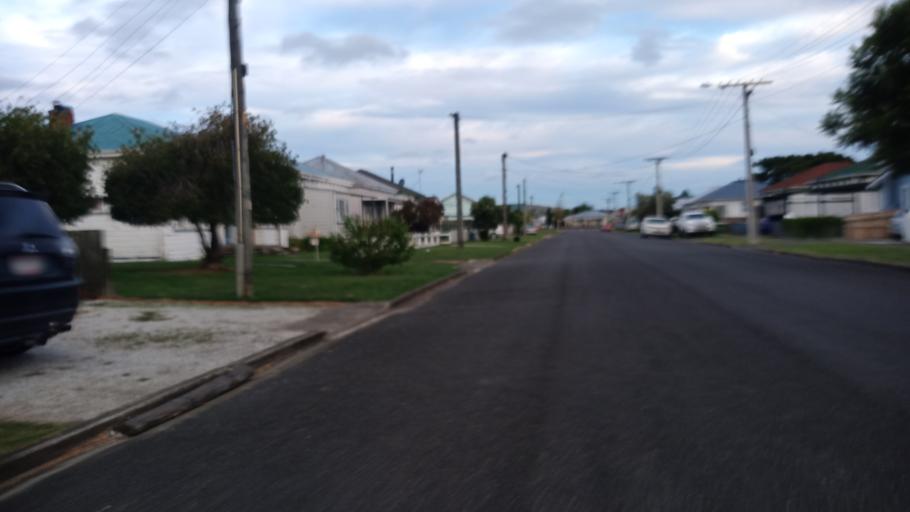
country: NZ
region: Gisborne
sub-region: Gisborne District
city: Gisborne
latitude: -38.6559
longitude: 178.0154
